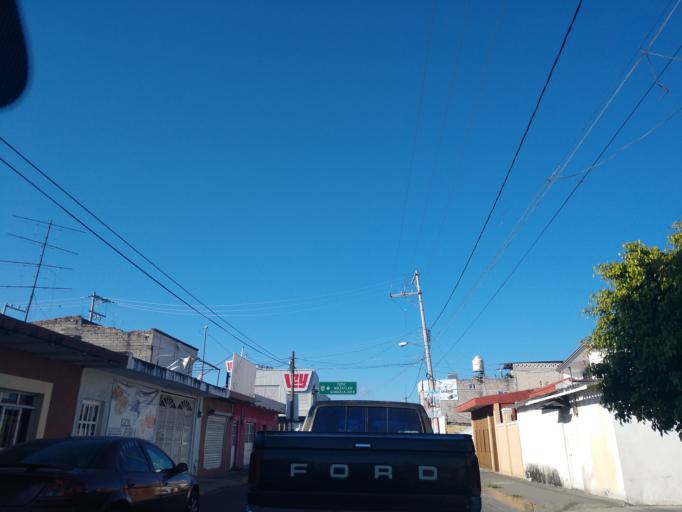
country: MX
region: Nayarit
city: Xalisco
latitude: 21.4509
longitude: -104.8977
